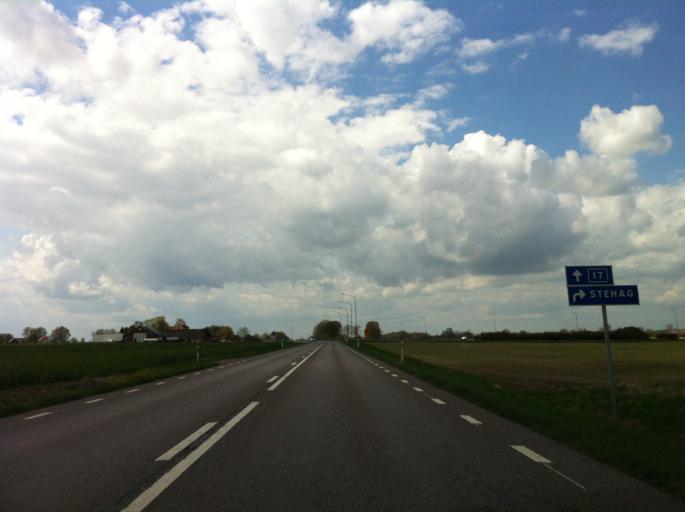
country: SE
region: Skane
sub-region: Eslovs Kommun
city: Stehag
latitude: 55.8549
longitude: 13.3750
